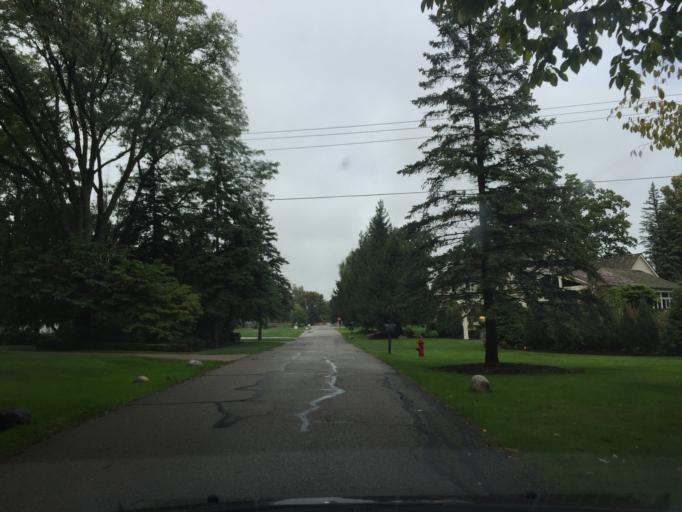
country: US
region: Michigan
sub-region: Oakland County
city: Bingham Farms
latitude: 42.5390
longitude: -83.2793
